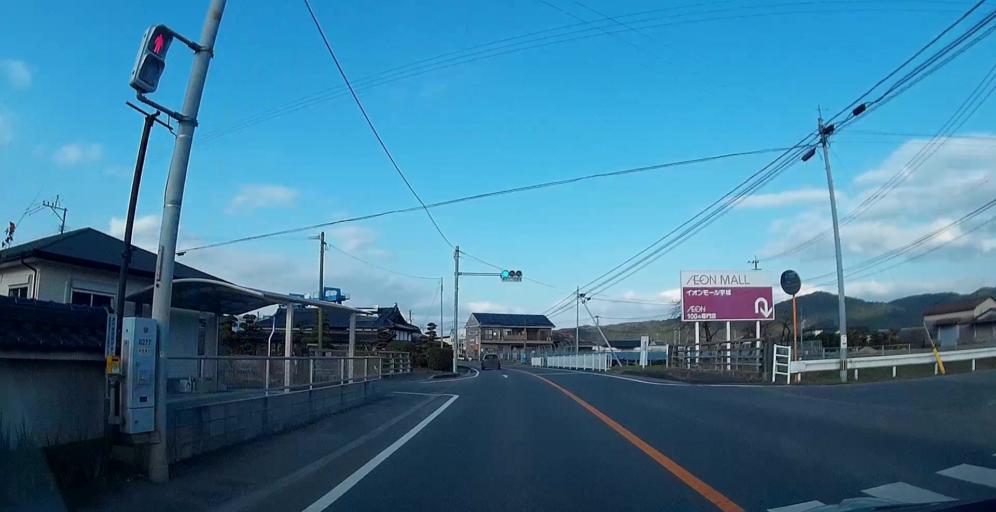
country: JP
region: Kumamoto
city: Matsubase
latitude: 32.6087
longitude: 130.7053
